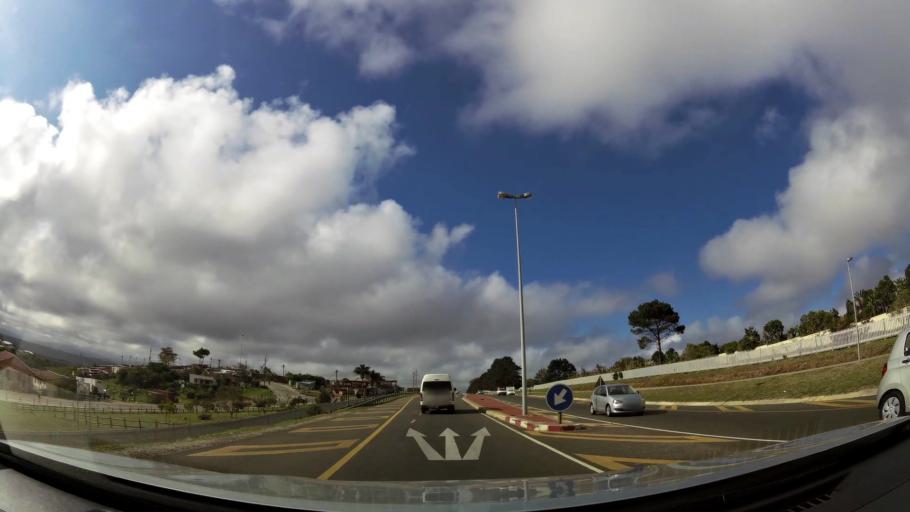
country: ZA
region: Western Cape
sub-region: Eden District Municipality
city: Plettenberg Bay
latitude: -34.0538
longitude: 23.3469
